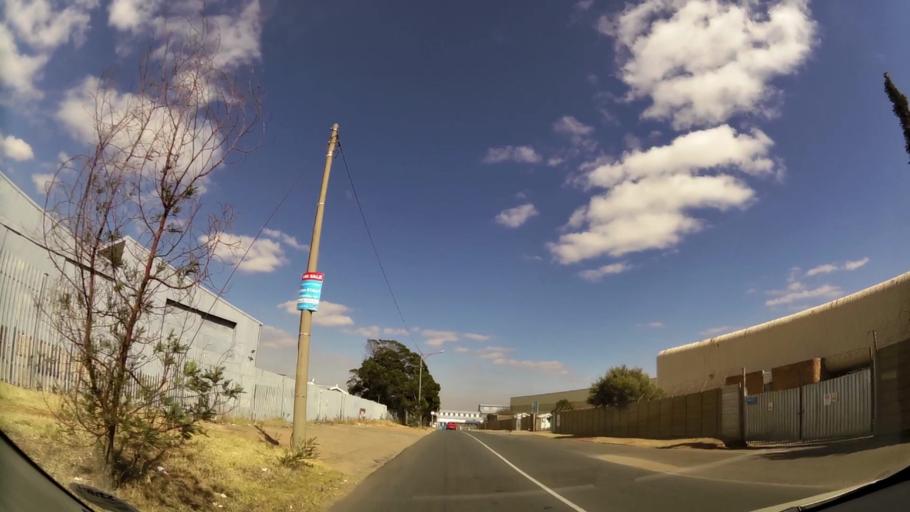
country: ZA
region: Gauteng
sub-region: West Rand District Municipality
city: Krugersdorp
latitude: -26.1136
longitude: 27.8100
